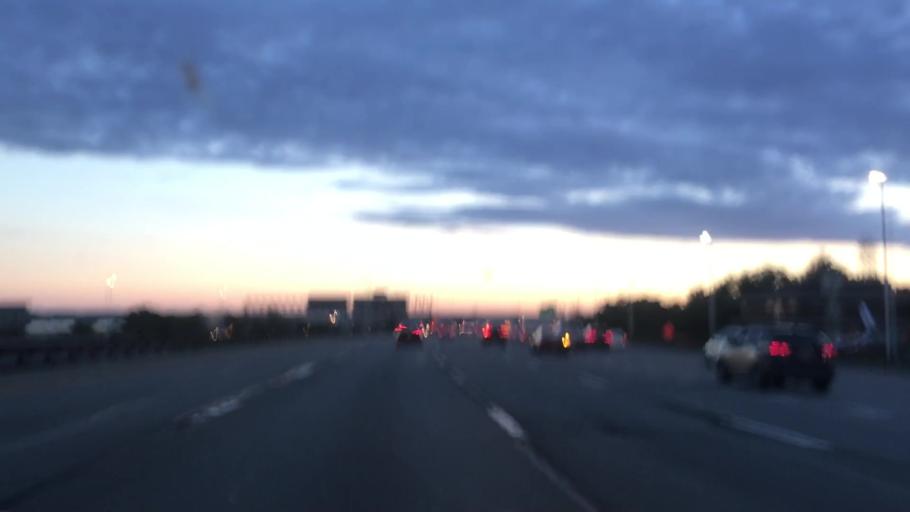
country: US
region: New Jersey
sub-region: Middlesex County
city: South Amboy
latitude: 40.4874
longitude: -74.3024
